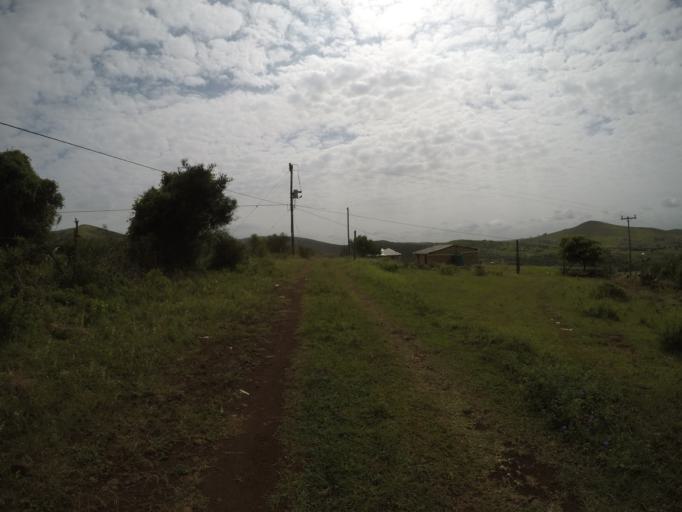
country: ZA
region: KwaZulu-Natal
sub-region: uThungulu District Municipality
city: Empangeni
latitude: -28.6189
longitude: 31.9073
